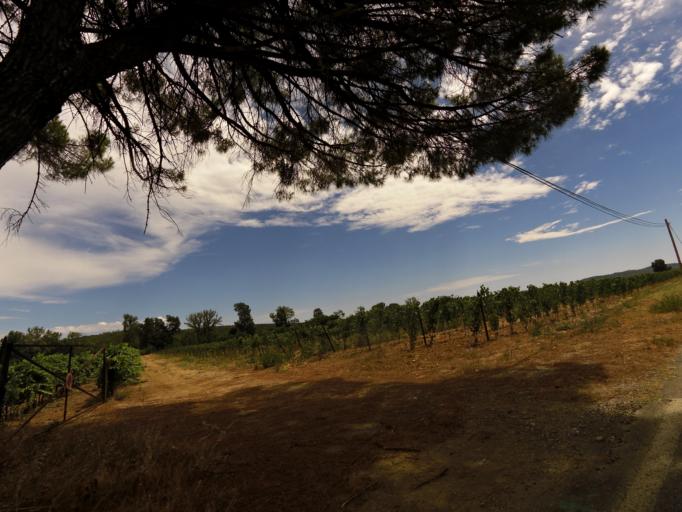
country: FR
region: Languedoc-Roussillon
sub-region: Departement du Gard
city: Quissac
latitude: 43.8983
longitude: 4.0017
